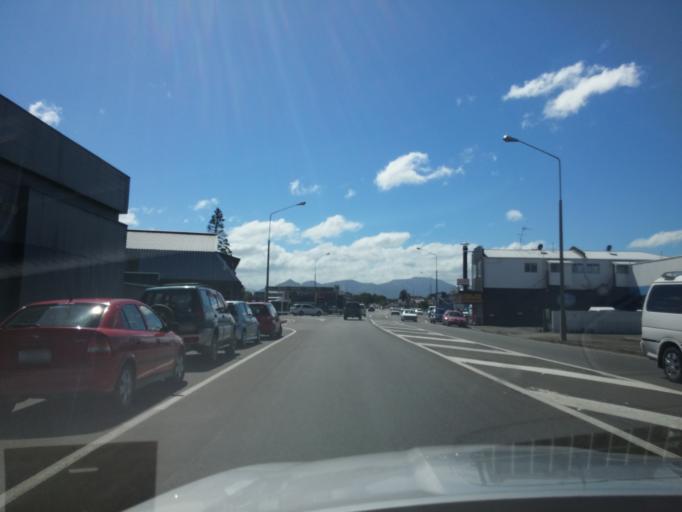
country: NZ
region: Marlborough
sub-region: Marlborough District
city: Blenheim
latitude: -41.5068
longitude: 173.9595
